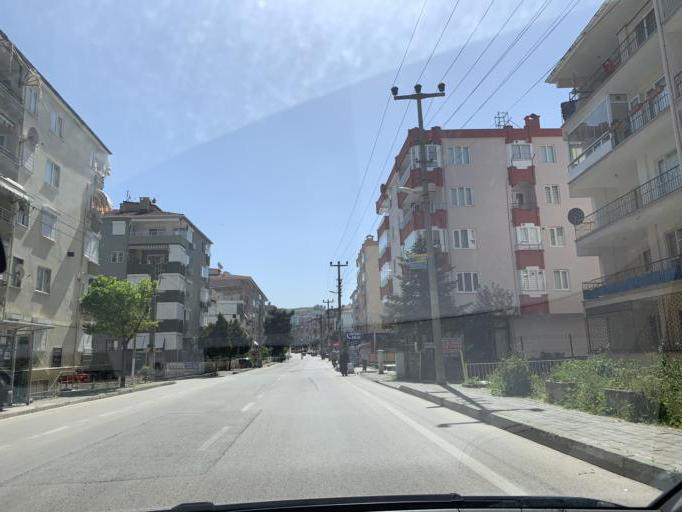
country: TR
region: Bursa
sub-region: Mudanya
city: Mudanya
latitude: 40.3557
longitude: 28.9222
